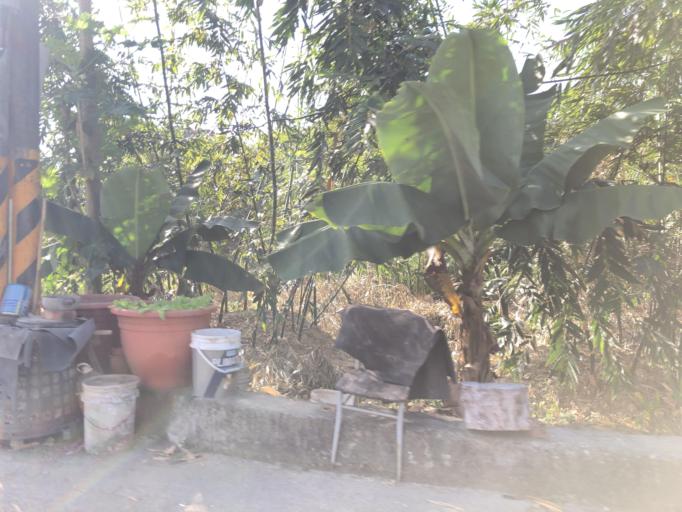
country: TW
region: Taiwan
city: Yujing
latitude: 23.0107
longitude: 120.3858
